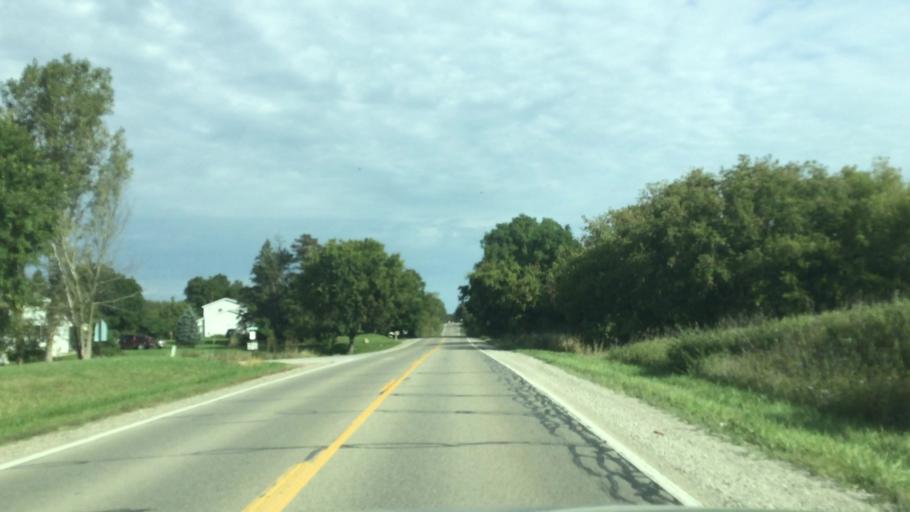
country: US
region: Michigan
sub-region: Livingston County
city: Howell
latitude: 42.6353
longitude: -83.8757
